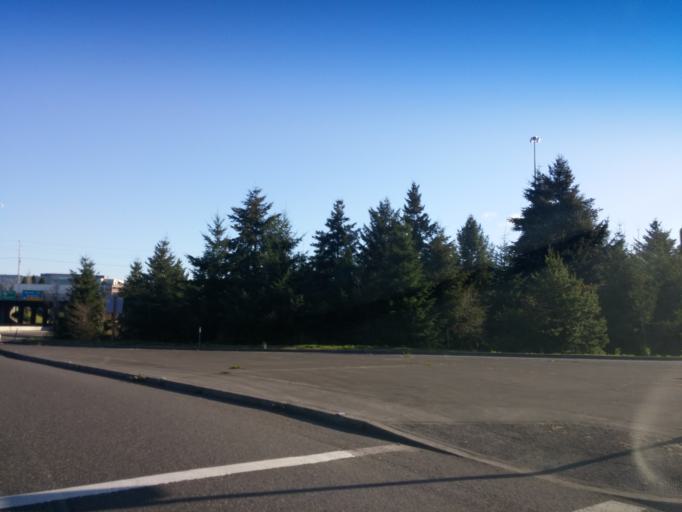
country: US
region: Oregon
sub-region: Washington County
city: West Haven-Sylvan
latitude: 45.5067
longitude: -122.7784
